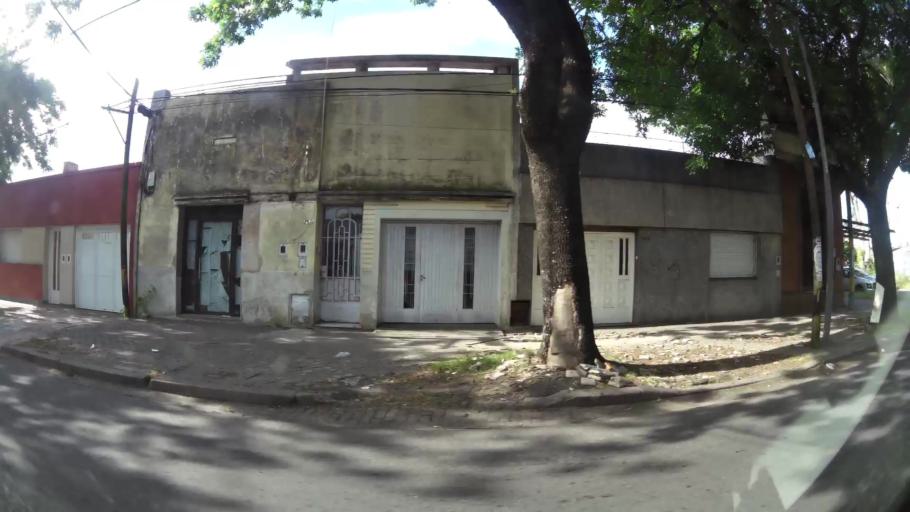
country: AR
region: Santa Fe
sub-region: Departamento de Rosario
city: Rosario
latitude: -32.9267
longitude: -60.6807
